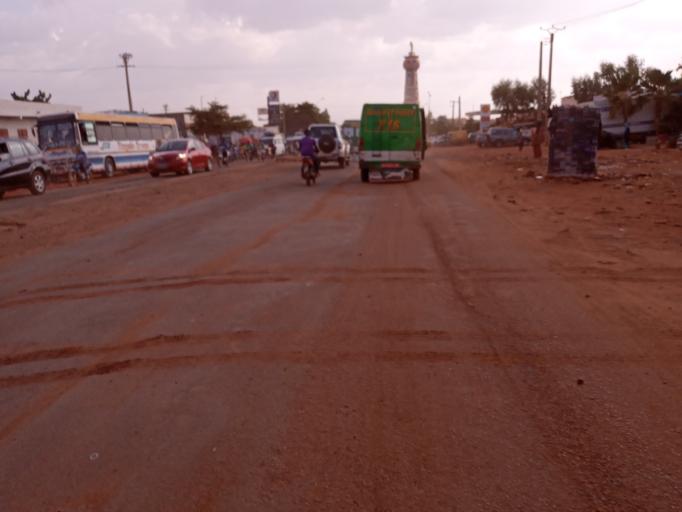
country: ML
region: Bamako
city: Bamako
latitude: 12.5872
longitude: -7.9427
